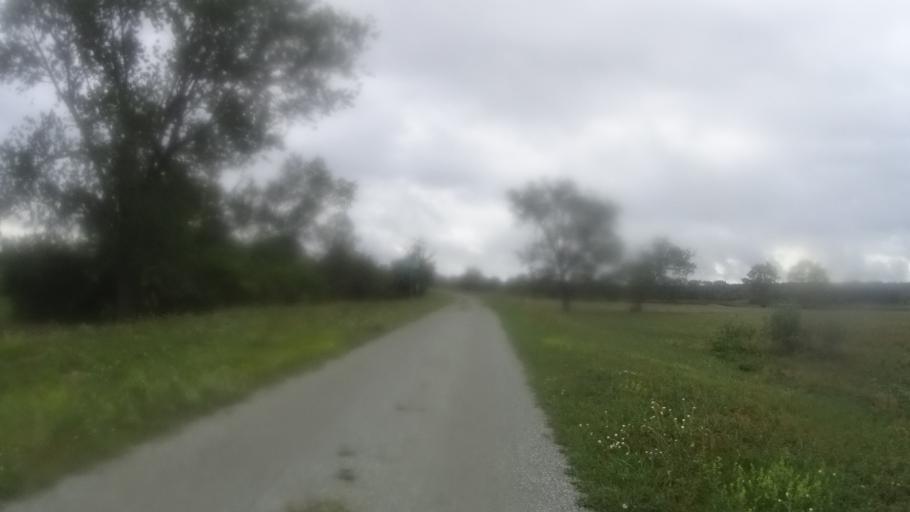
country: DE
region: Lower Saxony
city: Gorleben
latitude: 53.0580
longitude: 11.3441
